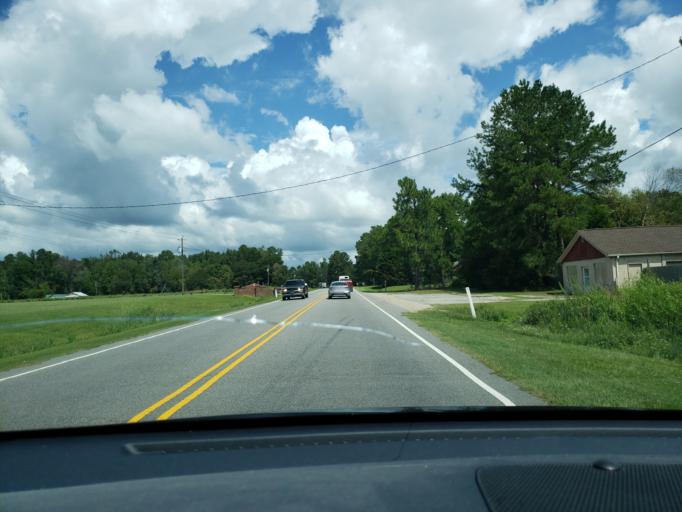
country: US
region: North Carolina
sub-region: Columbus County
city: Brunswick
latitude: 34.2649
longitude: -78.7426
